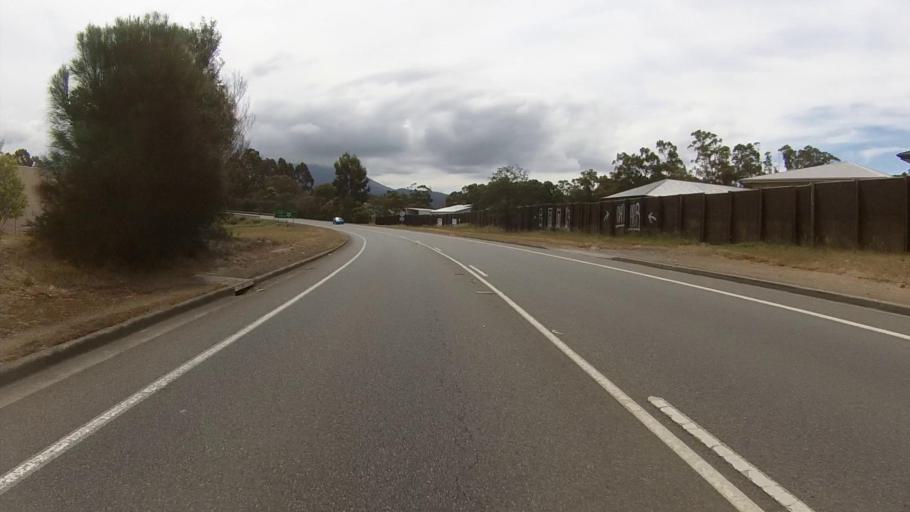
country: AU
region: Tasmania
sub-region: Kingborough
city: Kingston
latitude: -42.9902
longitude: 147.2940
